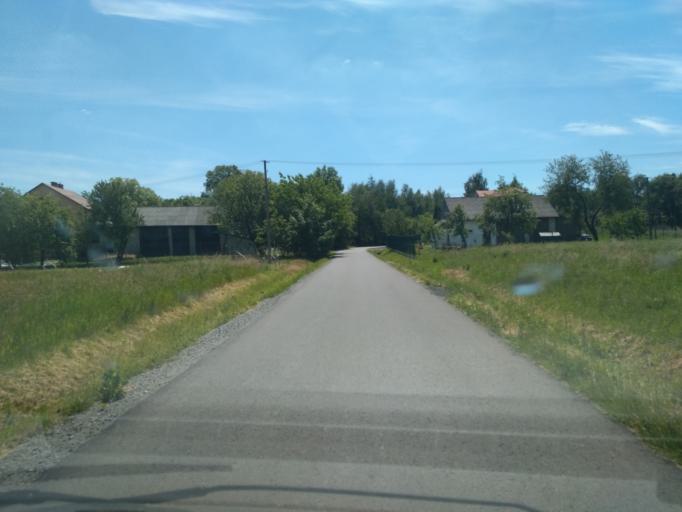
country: PL
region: Subcarpathian Voivodeship
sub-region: Powiat rzeszowski
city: Lubenia
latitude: 49.9158
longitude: 21.9157
